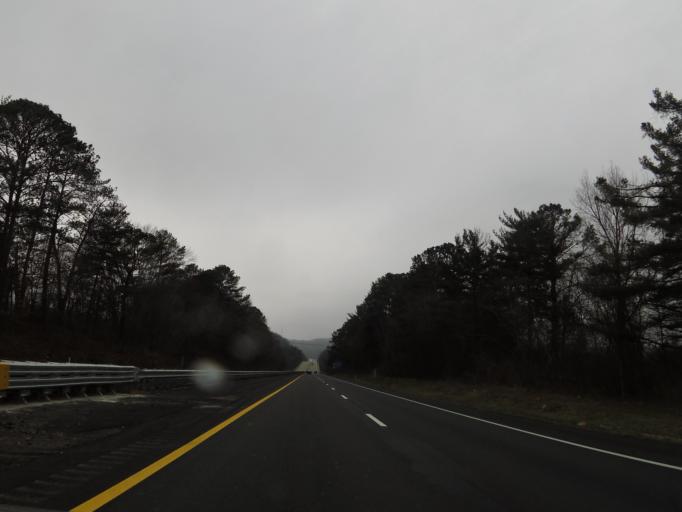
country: US
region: Tennessee
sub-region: Roane County
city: Kingston
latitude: 35.8866
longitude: -84.5186
